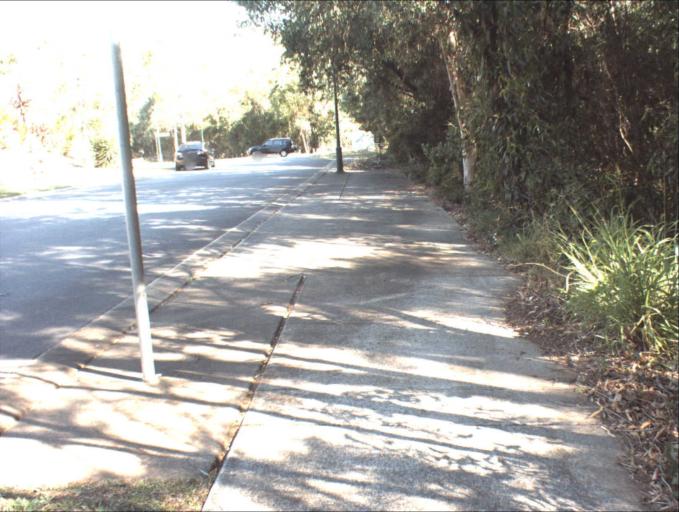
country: AU
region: Queensland
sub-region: Logan
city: Slacks Creek
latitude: -27.6319
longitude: 153.1585
